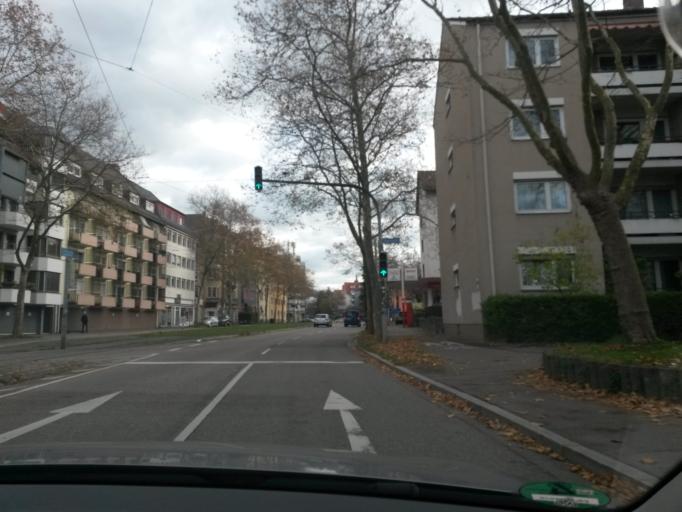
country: DE
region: Baden-Wuerttemberg
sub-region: Freiburg Region
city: Freiburg
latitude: 48.0035
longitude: 7.8375
